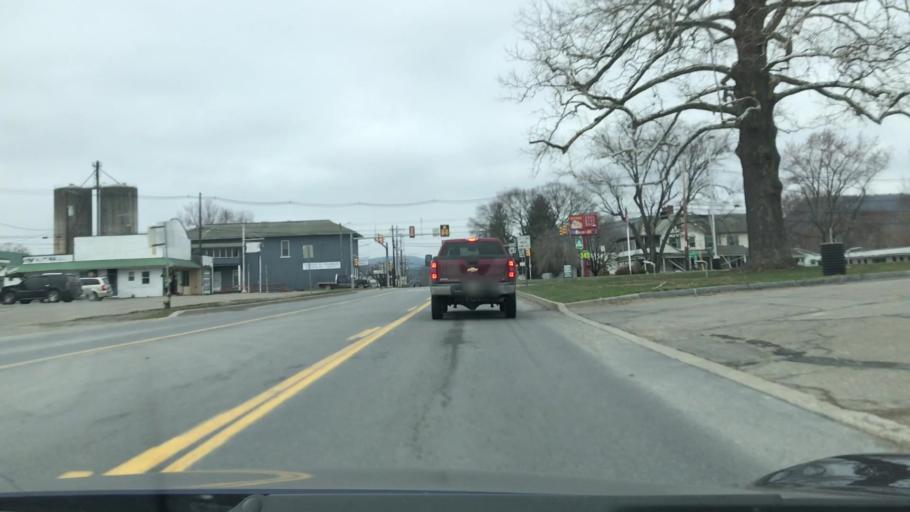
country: US
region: Pennsylvania
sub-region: Bradford County
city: Towanda
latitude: 41.7743
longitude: -76.3983
